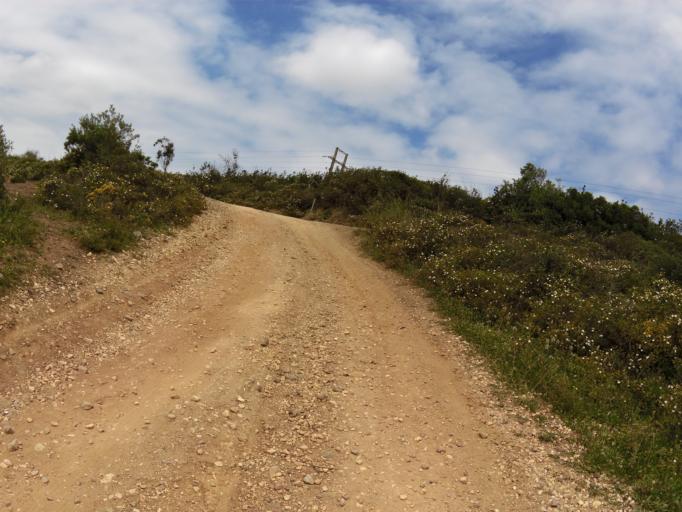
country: PT
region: Faro
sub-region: Vila do Bispo
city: Vila do Bispo
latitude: 37.0864
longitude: -8.8945
